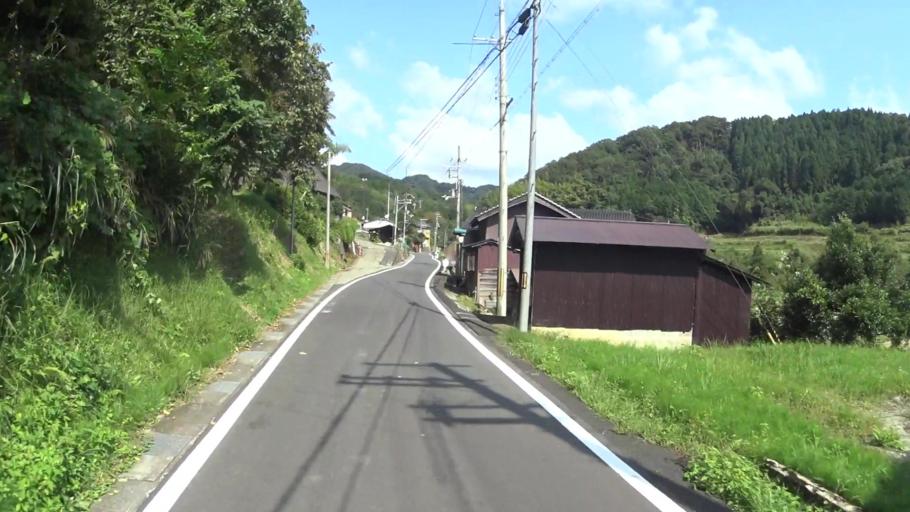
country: JP
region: Kyoto
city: Miyazu
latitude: 35.6312
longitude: 135.2315
